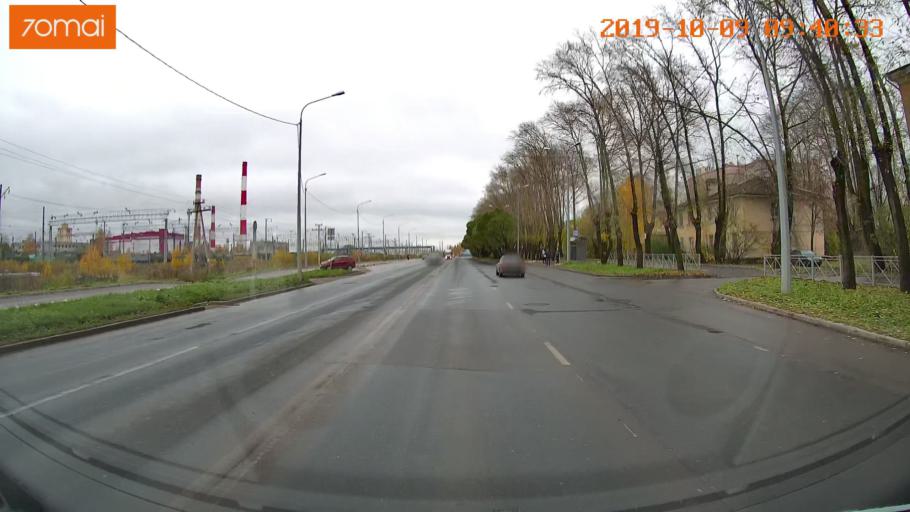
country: RU
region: Vologda
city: Vologda
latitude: 59.1948
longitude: 39.9274
